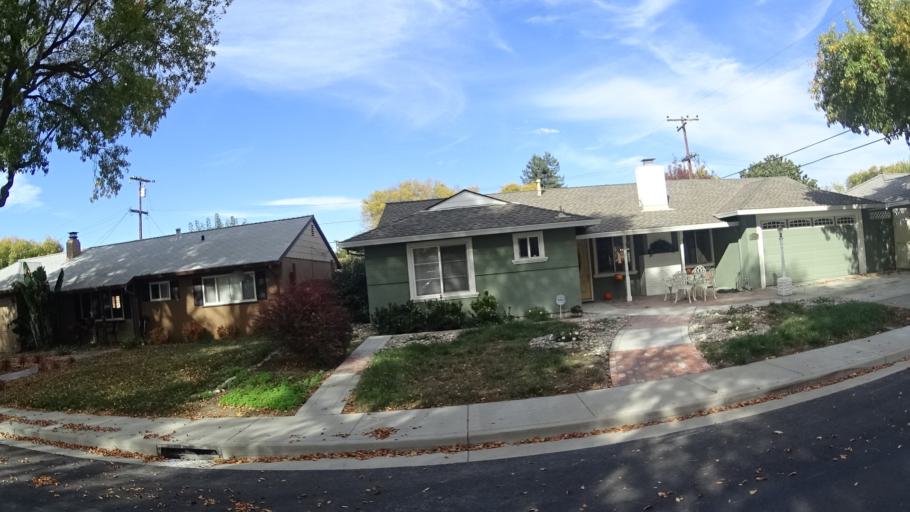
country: US
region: California
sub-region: Santa Clara County
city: Santa Clara
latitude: 37.3545
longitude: -121.9669
